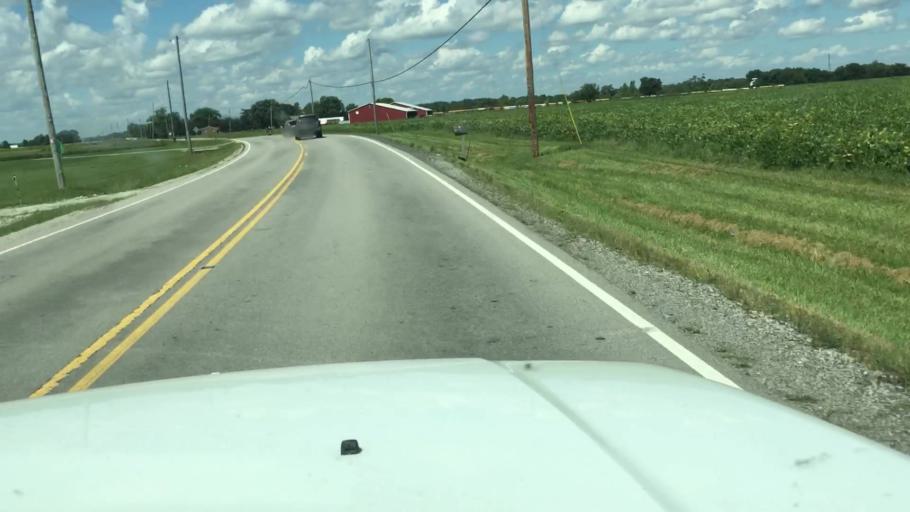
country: US
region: Ohio
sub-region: Madison County
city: Mount Sterling
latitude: 39.7398
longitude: -83.2763
